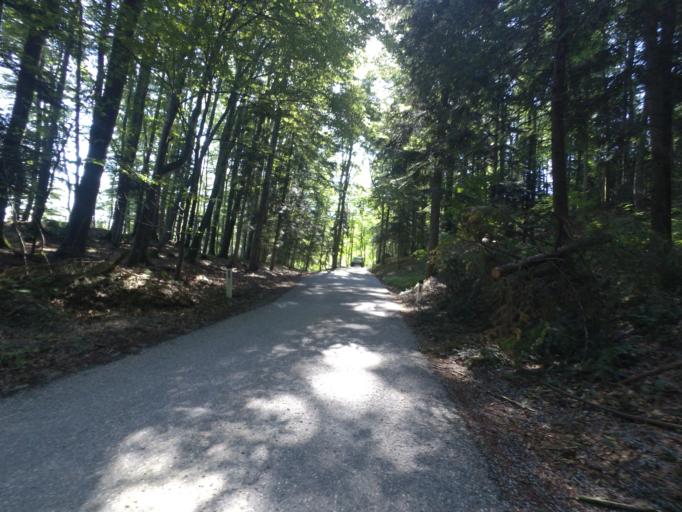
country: AT
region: Salzburg
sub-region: Politischer Bezirk Salzburg-Umgebung
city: Elsbethen
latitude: 47.7565
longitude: 13.1054
